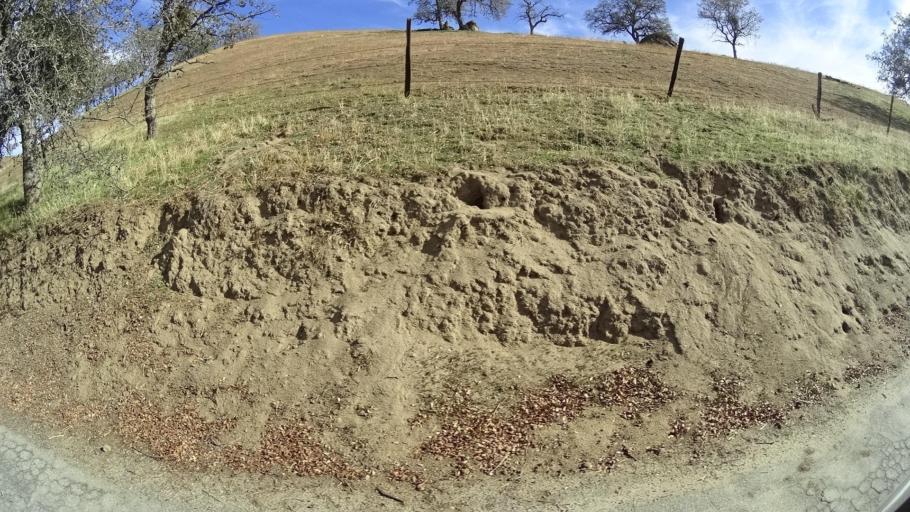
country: US
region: California
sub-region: Kern County
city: Oildale
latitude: 35.5669
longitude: -118.7987
